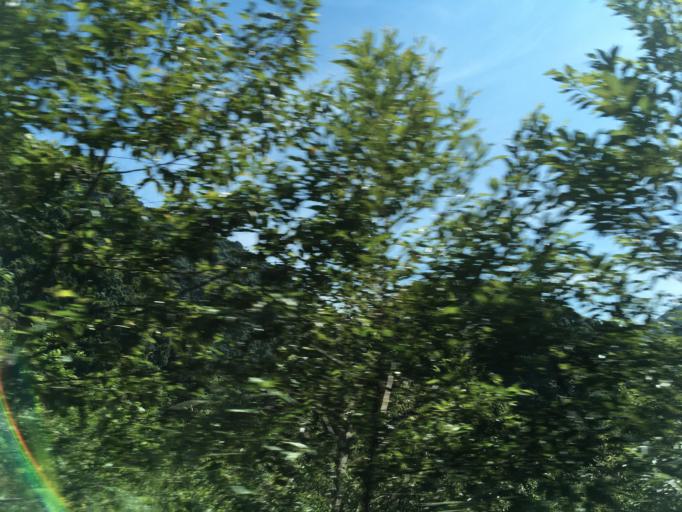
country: TW
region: Taiwan
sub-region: Yilan
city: Yilan
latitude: 24.4198
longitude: 121.7323
